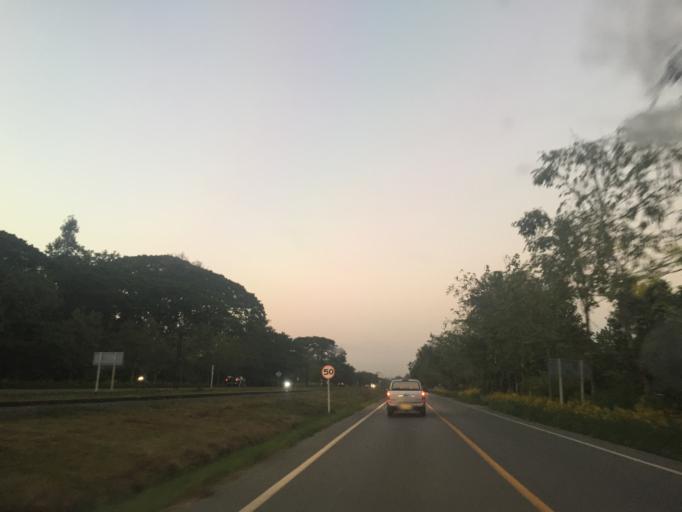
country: TH
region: Chiang Mai
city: Saraphi
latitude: 18.6942
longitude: 99.0456
